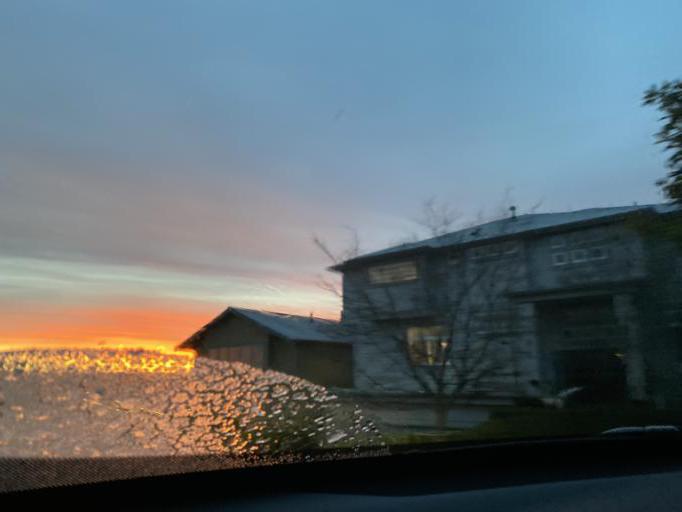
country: US
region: Washington
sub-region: King County
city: Seattle
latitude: 47.6302
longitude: -122.4008
